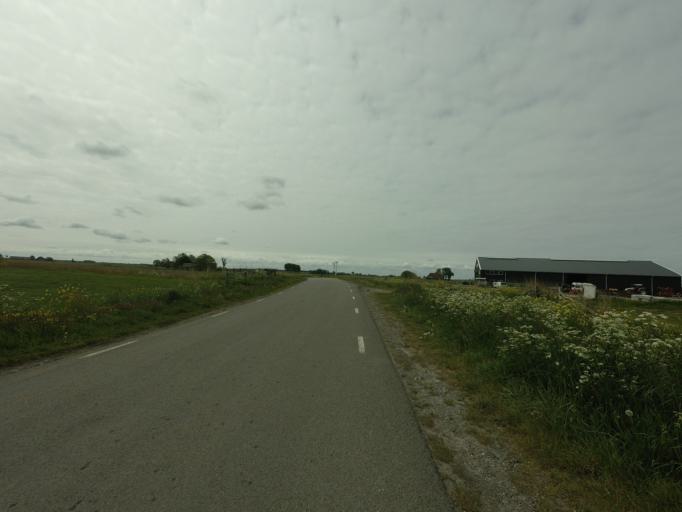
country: NL
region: Friesland
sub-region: Sudwest Fryslan
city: Koudum
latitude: 52.9434
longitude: 5.4864
